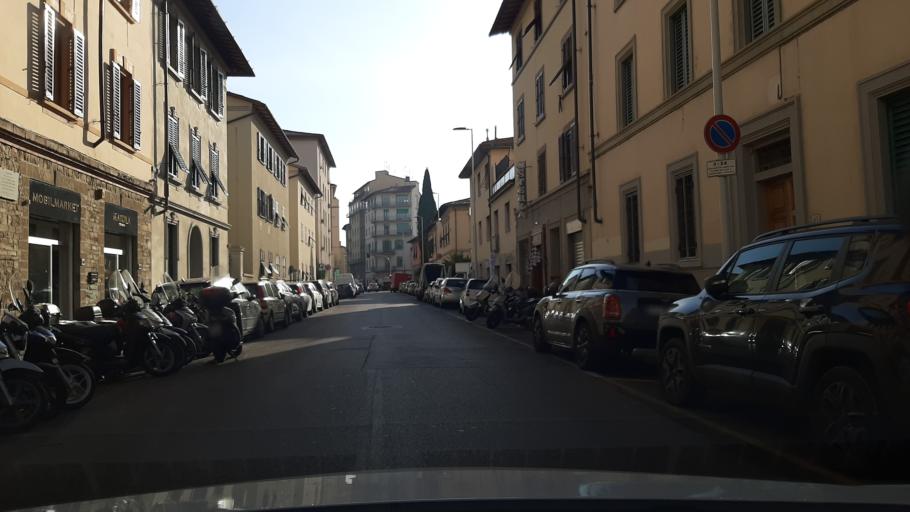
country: IT
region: Tuscany
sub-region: Province of Florence
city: Fiesole
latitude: 43.7830
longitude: 11.2854
